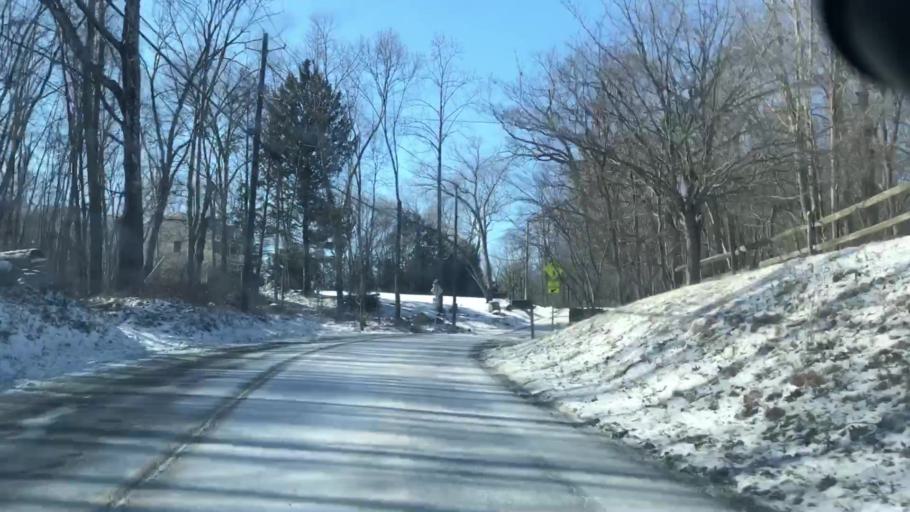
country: US
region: New York
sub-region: Putnam County
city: Carmel Hamlet
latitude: 41.3854
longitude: -73.6977
